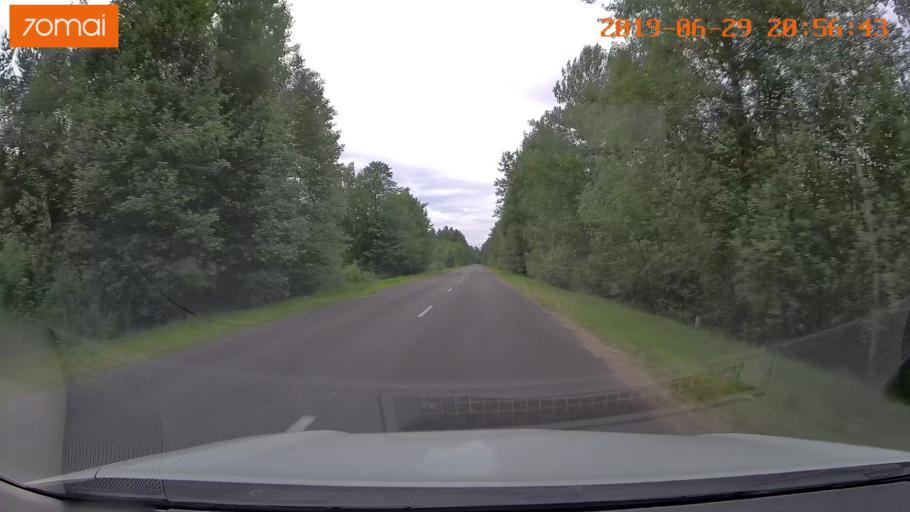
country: BY
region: Brest
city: Hantsavichy
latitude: 52.7090
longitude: 26.3686
